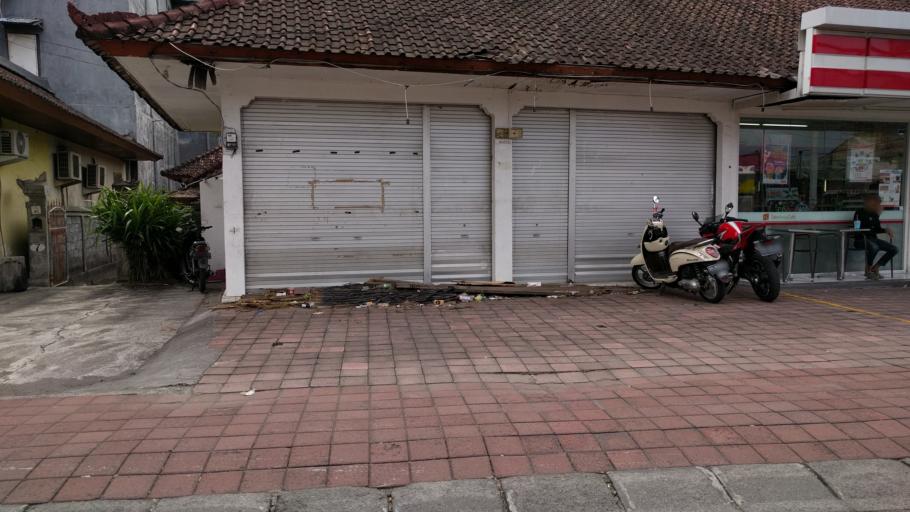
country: ID
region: Bali
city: Kuta
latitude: -8.6826
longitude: 115.1673
